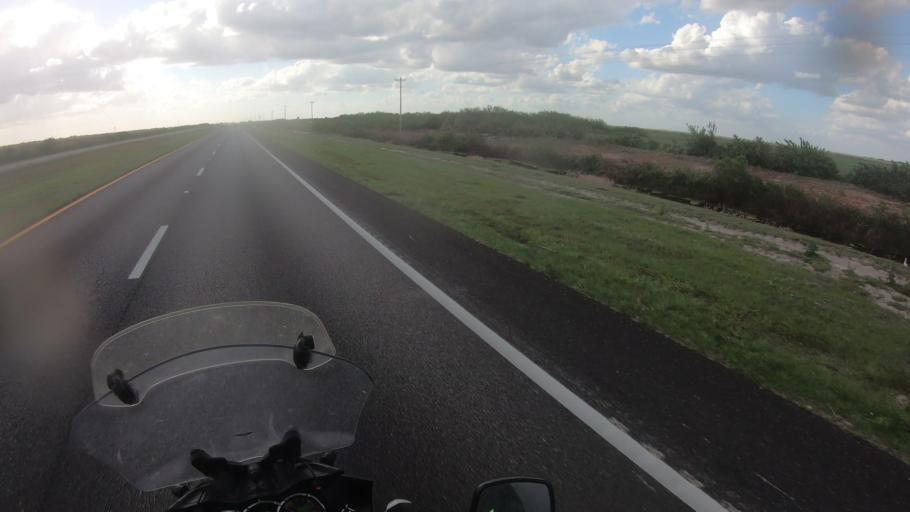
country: US
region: Florida
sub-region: Glades County
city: Moore Haven
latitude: 26.8334
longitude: -81.1658
